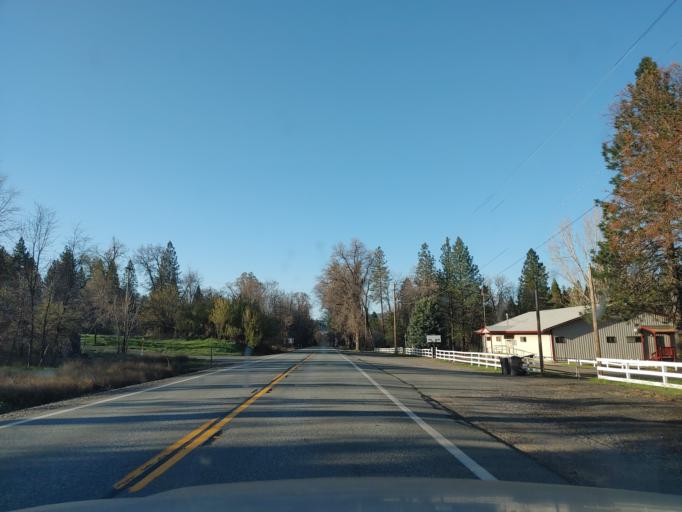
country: US
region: California
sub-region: Shasta County
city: Burney
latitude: 40.8109
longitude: -121.9393
